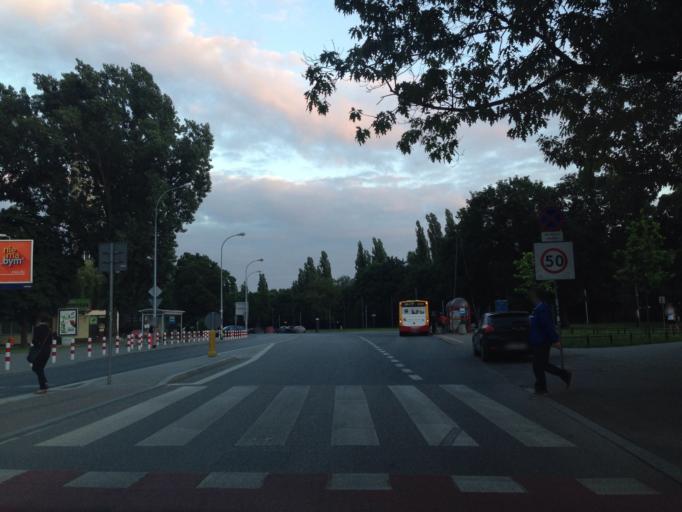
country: PL
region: Masovian Voivodeship
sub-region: Warszawa
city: Praga Polnoc
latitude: 52.2632
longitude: 21.0217
